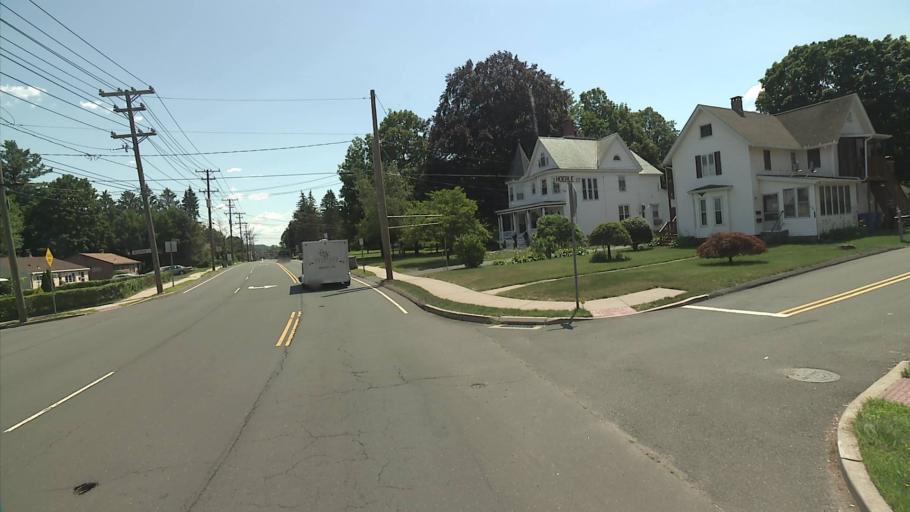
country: US
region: Connecticut
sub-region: Hartford County
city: Plainville
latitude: 41.6698
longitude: -72.8792
